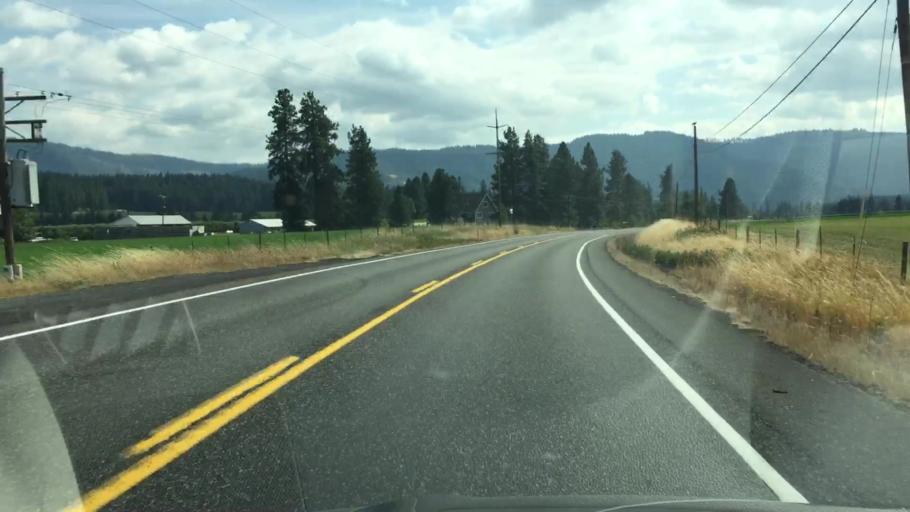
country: US
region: Washington
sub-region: Klickitat County
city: White Salmon
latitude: 45.8205
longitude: -121.4883
